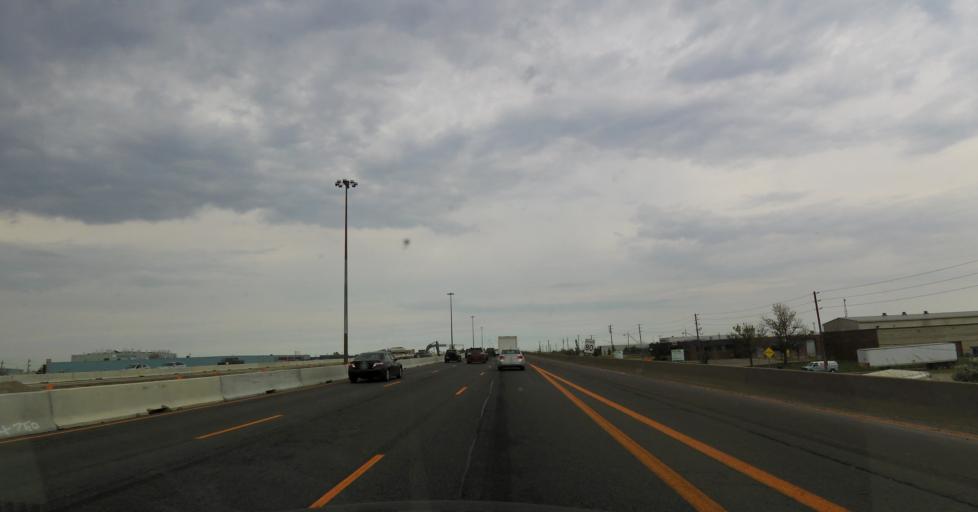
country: CA
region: Ontario
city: Brampton
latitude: 43.6995
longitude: -79.7305
